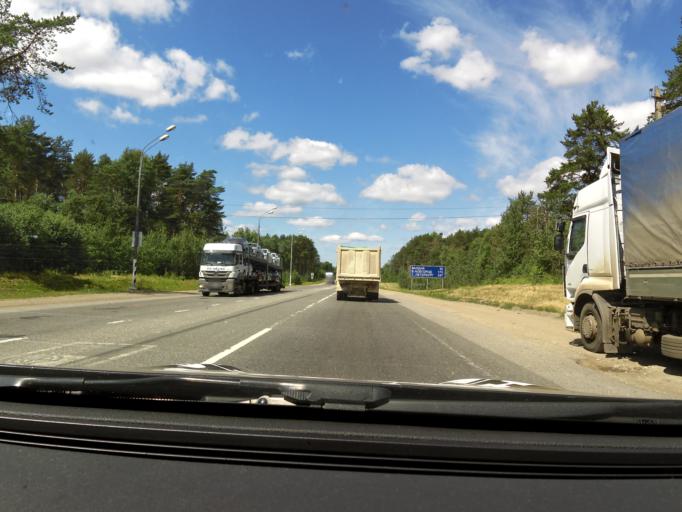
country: RU
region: Tverskaya
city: Vypolzovo
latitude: 57.8465
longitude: 33.7659
